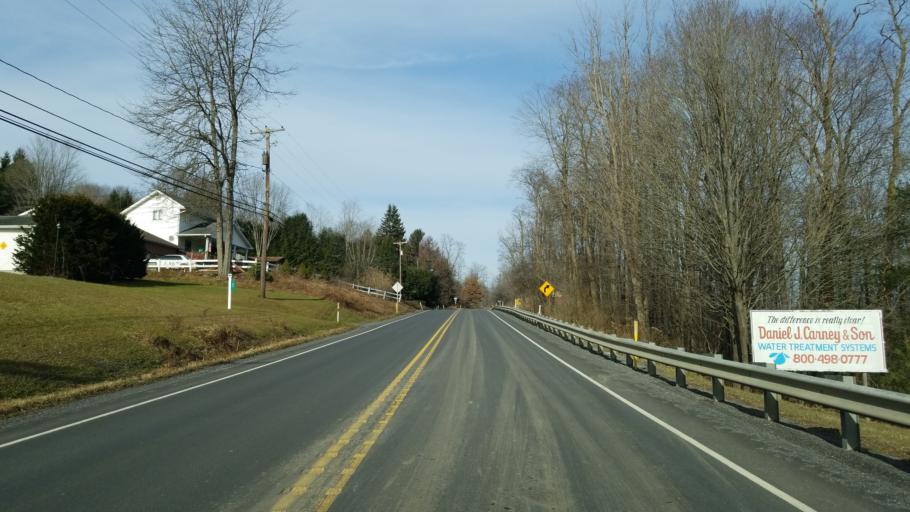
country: US
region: Pennsylvania
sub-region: Clearfield County
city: Curwensville
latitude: 40.9585
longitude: -78.6119
